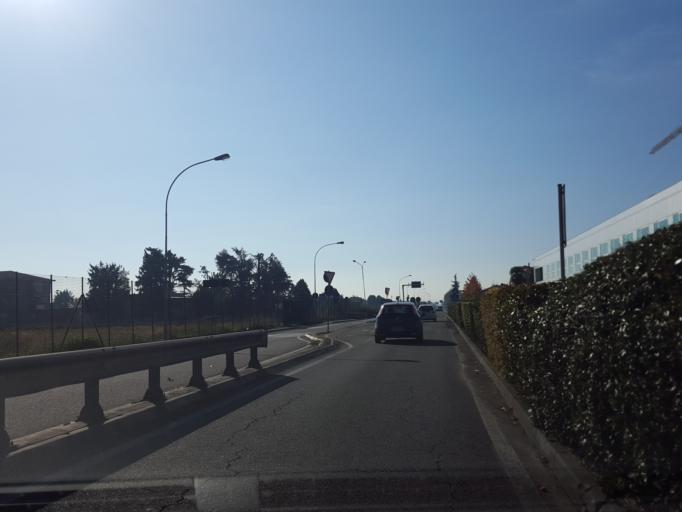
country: IT
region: Veneto
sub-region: Provincia di Vicenza
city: Brendola
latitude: 45.4927
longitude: 11.4289
